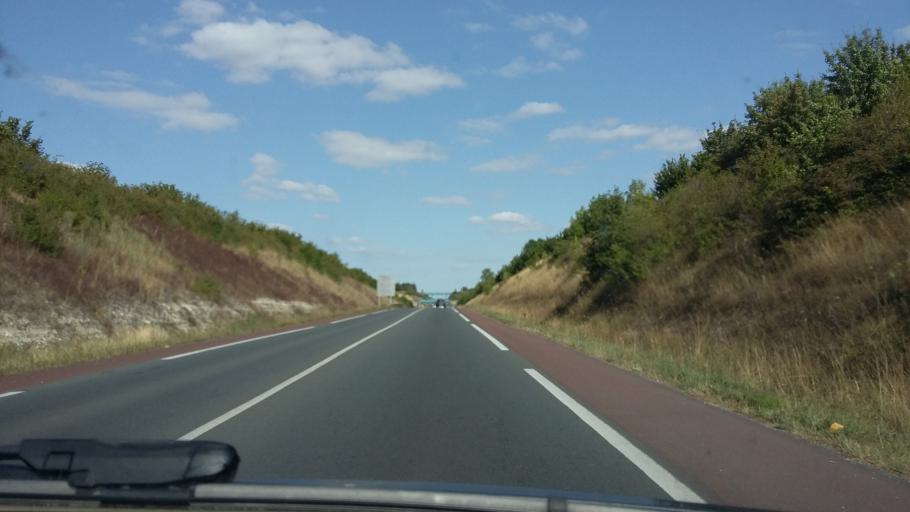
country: FR
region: Poitou-Charentes
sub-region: Departement de la Charente-Maritime
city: Saint-Jean-d'Angely
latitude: 45.9563
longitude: -0.5263
